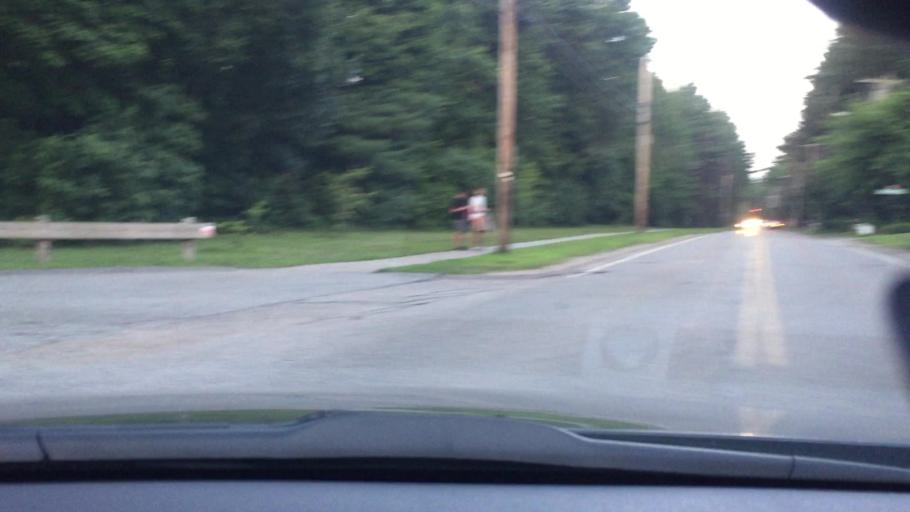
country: US
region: Massachusetts
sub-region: Norfolk County
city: Needham
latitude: 42.2719
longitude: -71.2243
